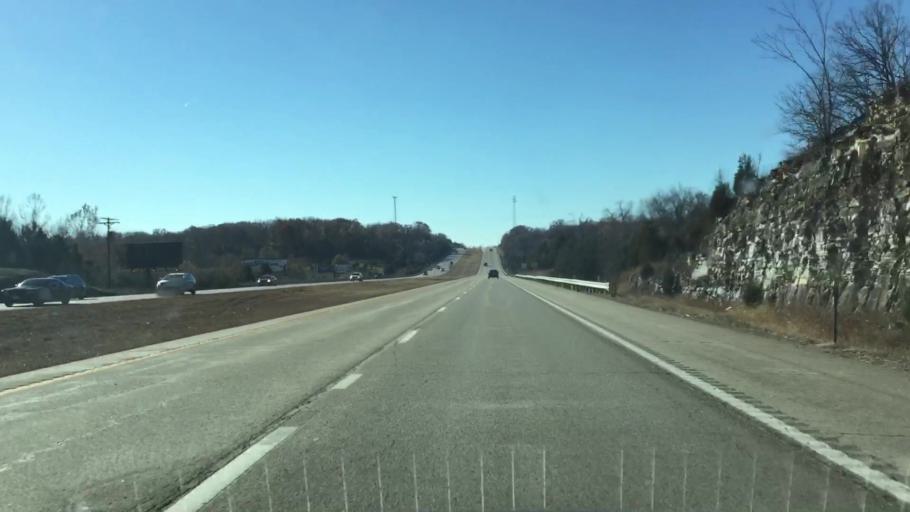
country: US
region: Missouri
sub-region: Cole County
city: Wardsville
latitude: 38.4930
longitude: -92.2696
